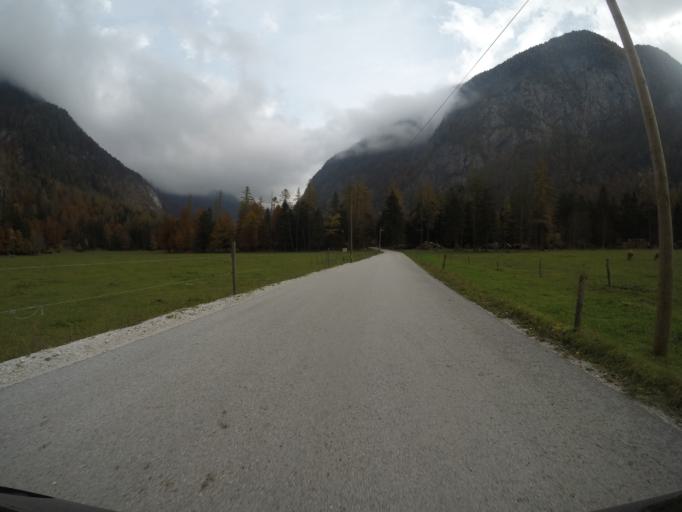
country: SI
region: Kranjska Gora
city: Mojstrana
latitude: 46.4313
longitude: 13.9430
